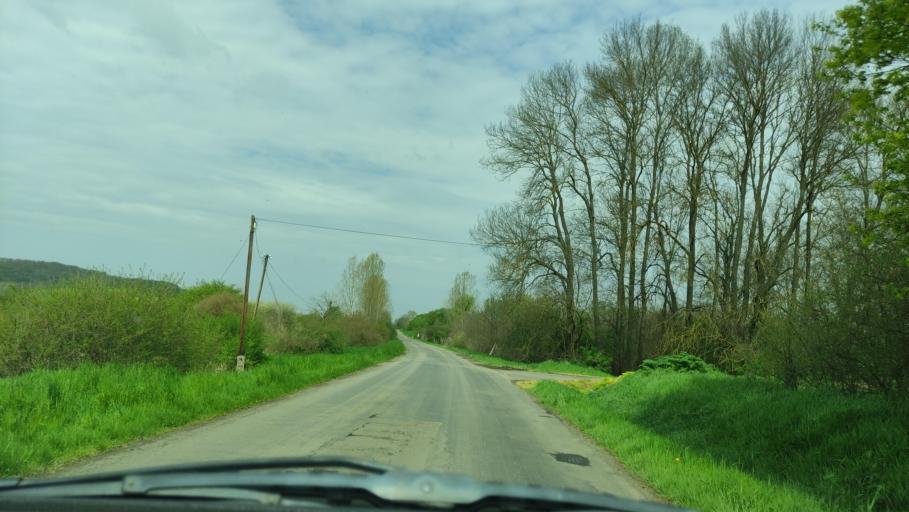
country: HU
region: Baranya
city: Magocs
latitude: 46.2964
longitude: 18.1802
